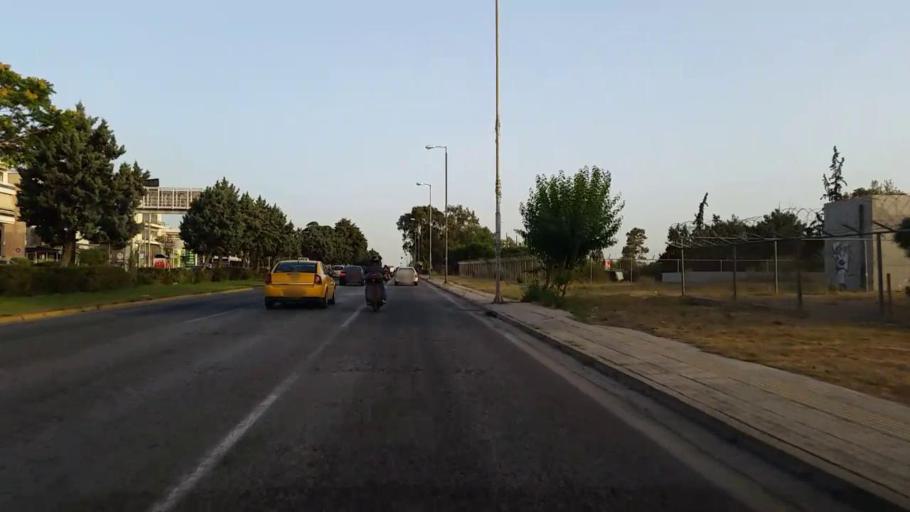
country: GR
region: Attica
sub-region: Nomarchia Athinas
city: Argyroupoli
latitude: 37.8982
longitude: 23.7464
